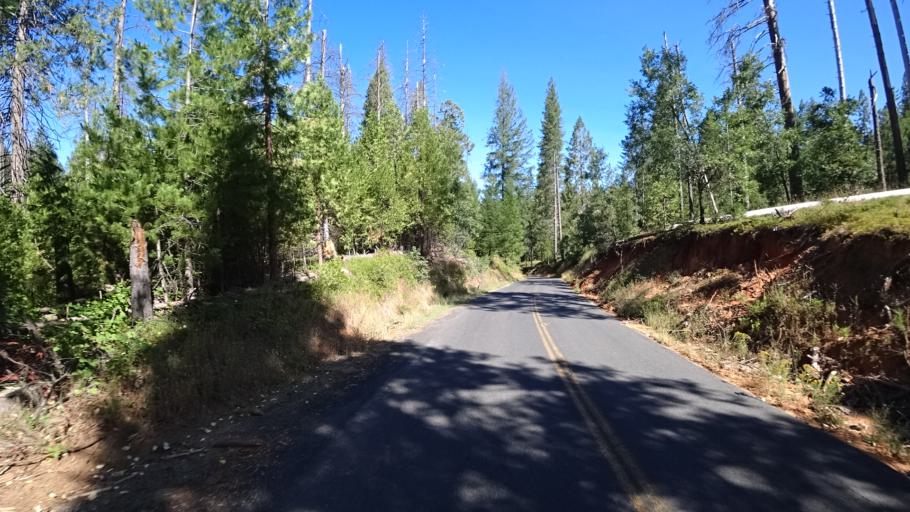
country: US
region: California
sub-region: Amador County
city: Pioneer
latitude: 38.3994
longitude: -120.4997
